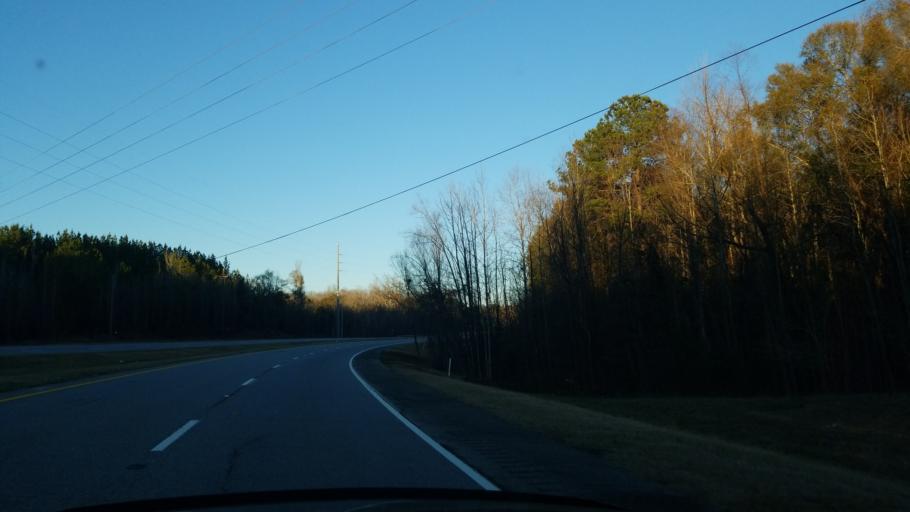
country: US
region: Georgia
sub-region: Chattahoochee County
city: Cusseta
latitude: 32.2702
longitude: -84.7853
